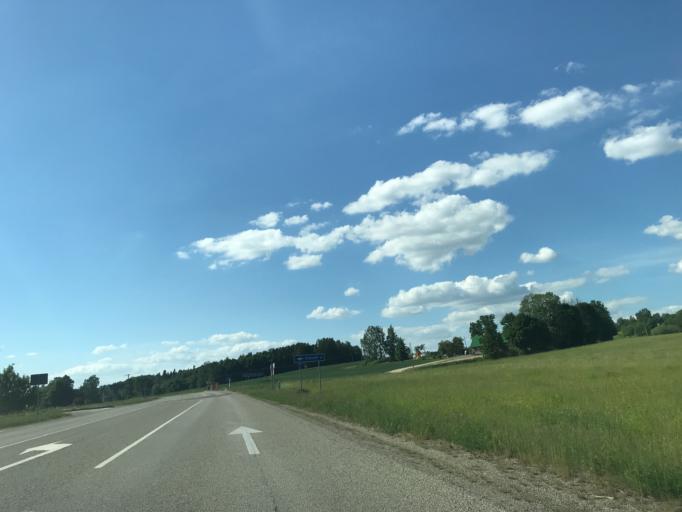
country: LV
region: Koknese
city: Koknese
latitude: 56.5576
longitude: 25.3633
